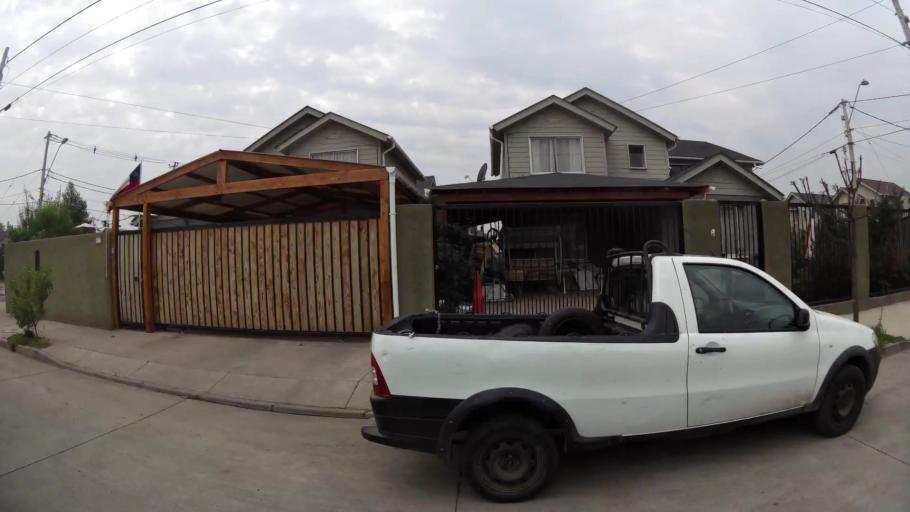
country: CL
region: Santiago Metropolitan
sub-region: Provincia de Chacabuco
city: Chicureo Abajo
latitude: -33.2113
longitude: -70.6908
